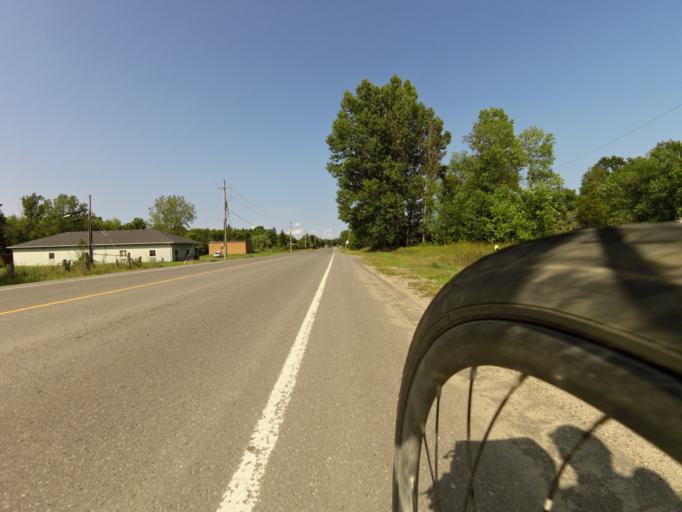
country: CA
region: Ontario
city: Skatepark
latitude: 44.2706
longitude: -76.7170
